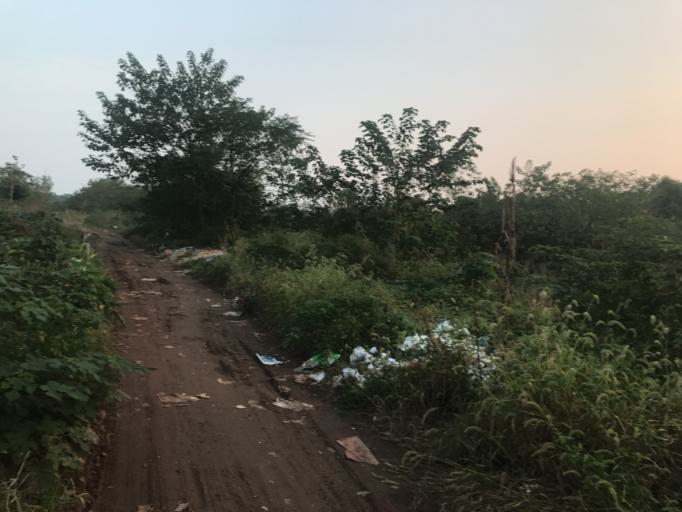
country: CN
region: Hubei
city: Anlu
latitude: 31.2651
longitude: 113.6522
